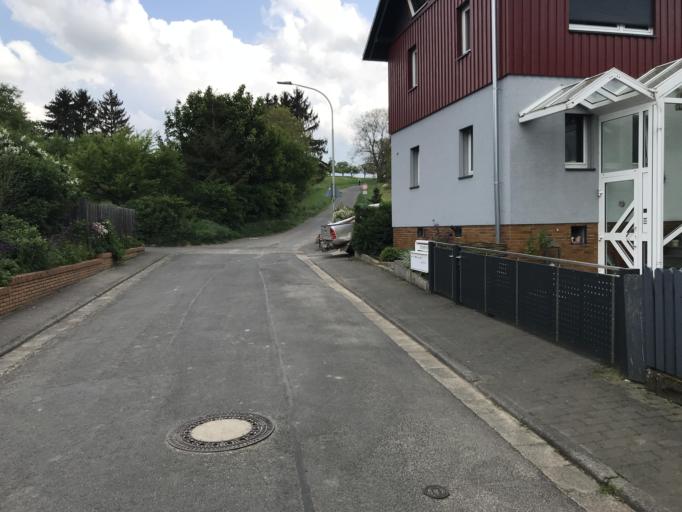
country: DE
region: Hesse
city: Budingen
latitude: 50.3076
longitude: 9.0880
